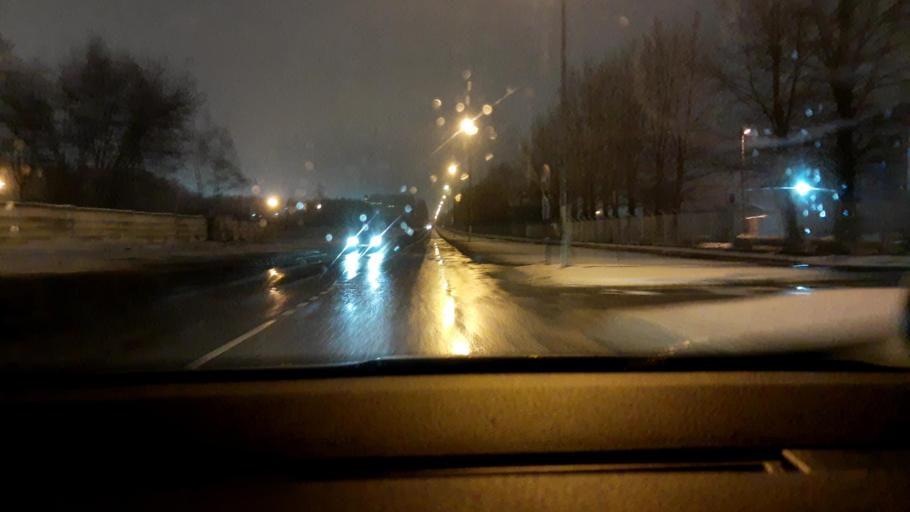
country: RU
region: Moskovskaya
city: Yakovlevskoye
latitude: 55.4244
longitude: 37.8815
